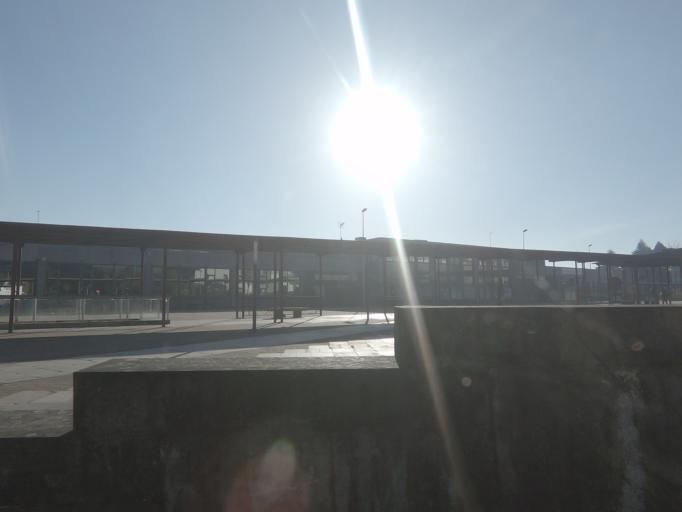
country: ES
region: Galicia
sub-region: Provincia da Coruna
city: Santiago de Compostela
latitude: 42.8877
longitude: -8.5342
